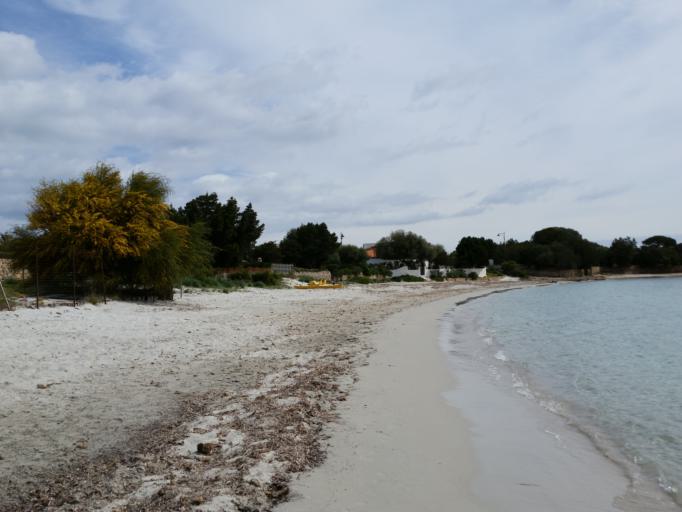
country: IT
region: Sardinia
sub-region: Provincia di Olbia-Tempio
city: Golfo Arnaci
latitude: 40.9472
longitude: 9.5742
